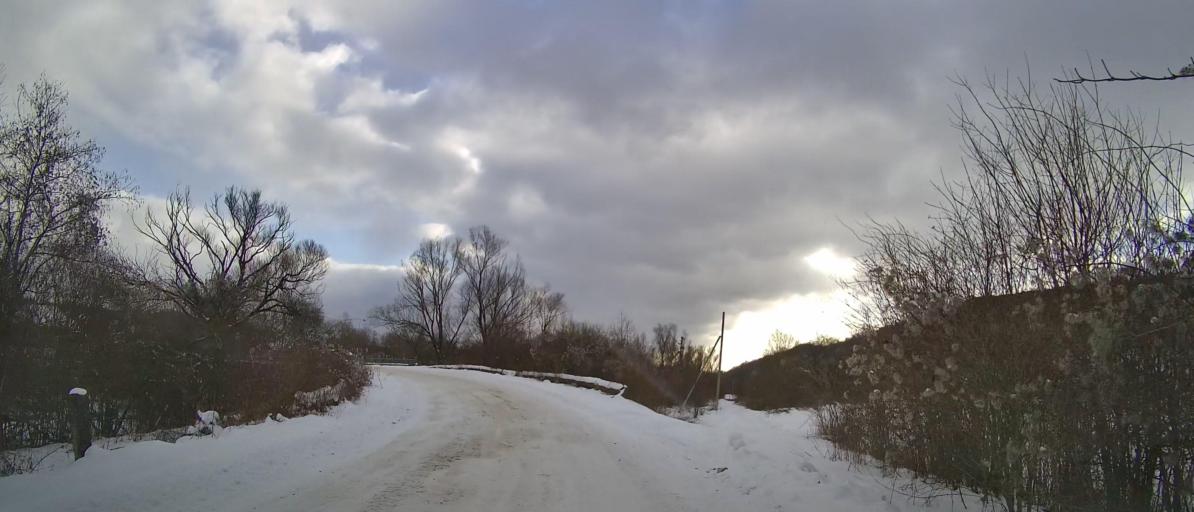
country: UA
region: Zakarpattia
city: Velykyi Bereznyi
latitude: 48.9222
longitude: 22.4627
